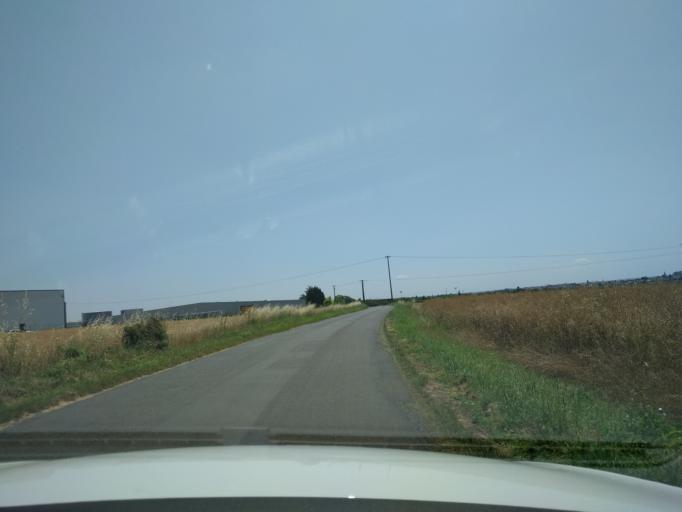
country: FR
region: Poitou-Charentes
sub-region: Departement des Deux-Sevres
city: Niort
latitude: 46.3518
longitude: -0.4464
